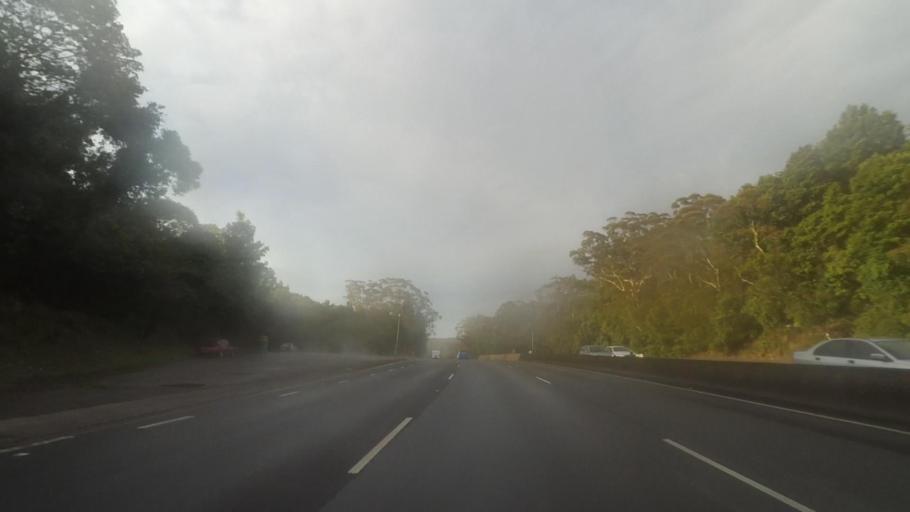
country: AU
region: New South Wales
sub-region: Wollongong
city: Mount Ousley
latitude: -34.3753
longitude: 150.8615
